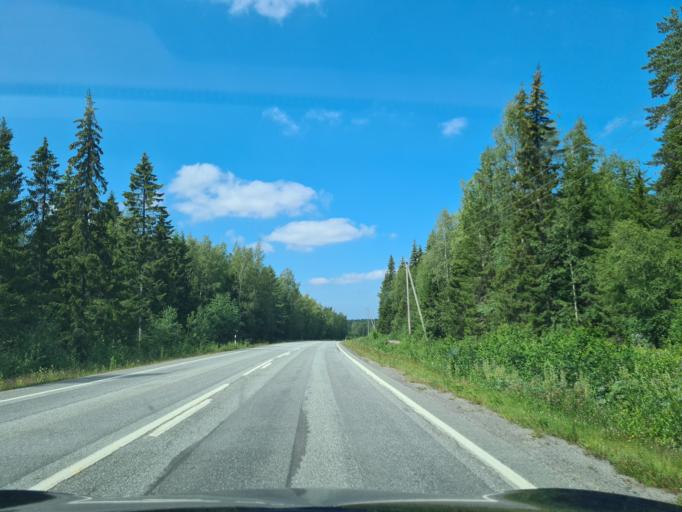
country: FI
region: Ostrobothnia
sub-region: Vaasa
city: Vaasa
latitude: 63.1838
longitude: 21.5681
